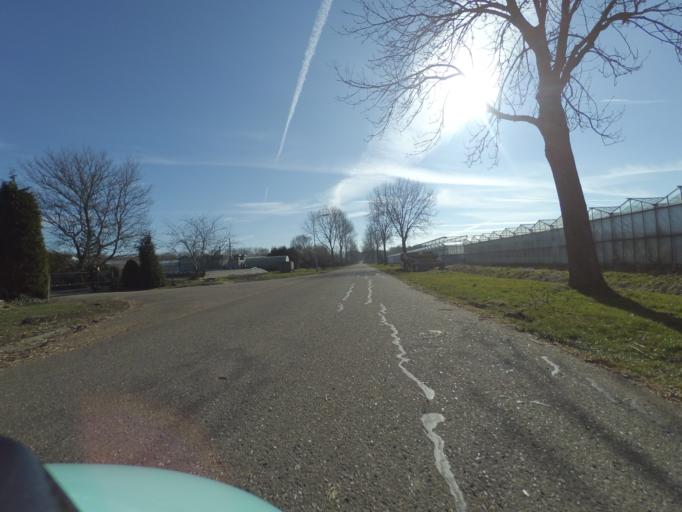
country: NL
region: Flevoland
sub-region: Gemeente Almere
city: Almere Stad
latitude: 52.4167
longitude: 5.2781
